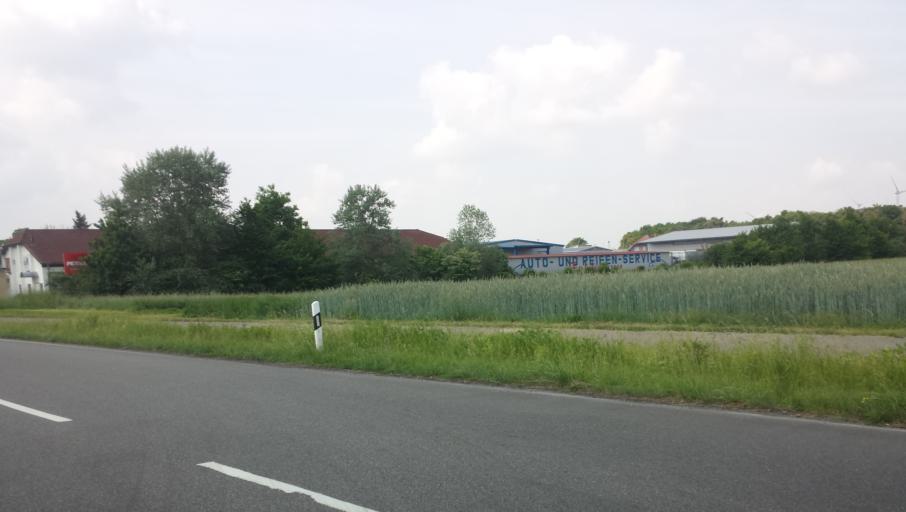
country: DE
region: Rheinland-Pfalz
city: Rheinzabern
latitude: 49.1238
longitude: 8.2808
